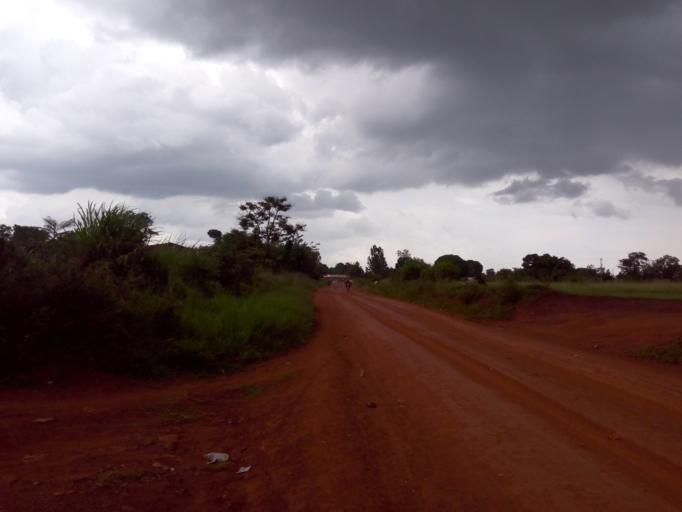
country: UG
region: Western Region
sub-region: Masindi District
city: Masindi
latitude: 1.6831
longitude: 31.7062
